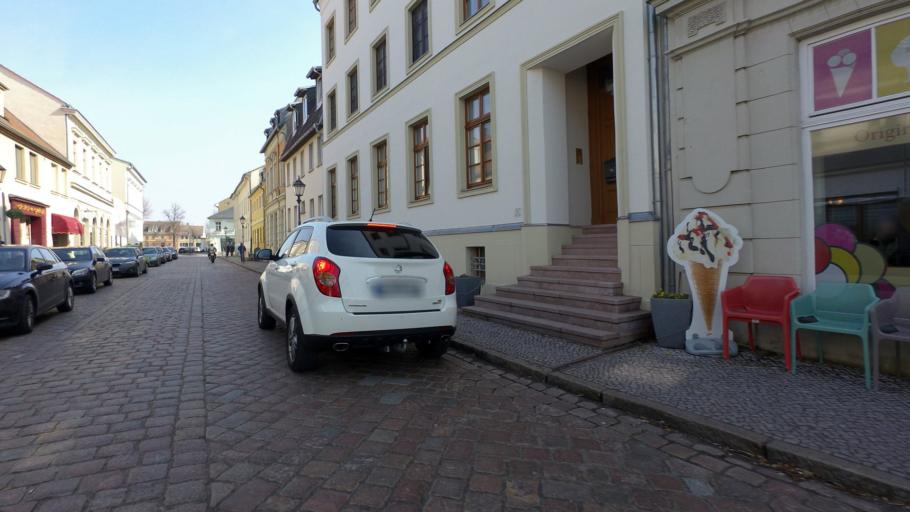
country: DE
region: Brandenburg
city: Werder
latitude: 52.3784
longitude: 12.9400
